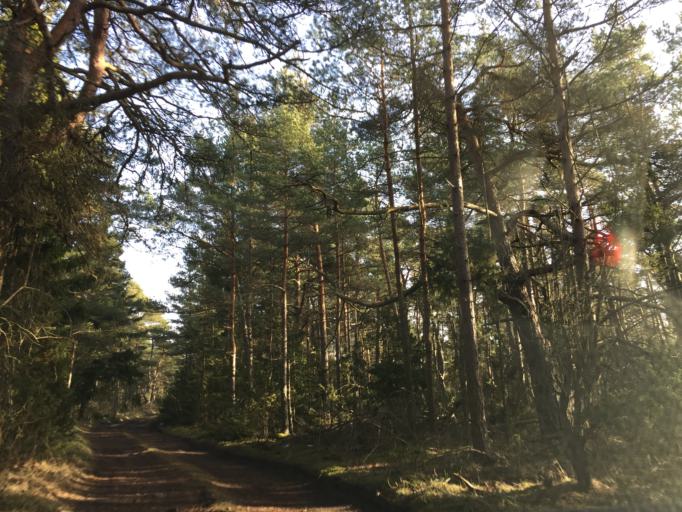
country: EE
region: Saare
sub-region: Kuressaare linn
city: Kuressaare
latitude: 58.3755
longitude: 22.0008
